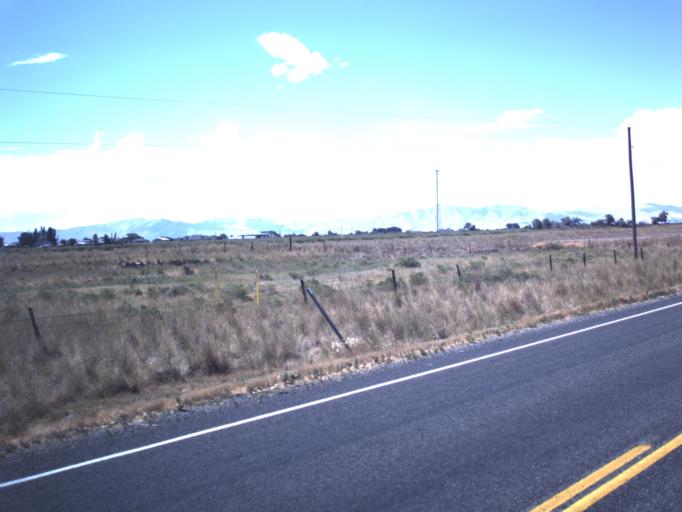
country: US
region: Utah
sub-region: Box Elder County
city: Honeyville
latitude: 41.5630
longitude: -112.1671
